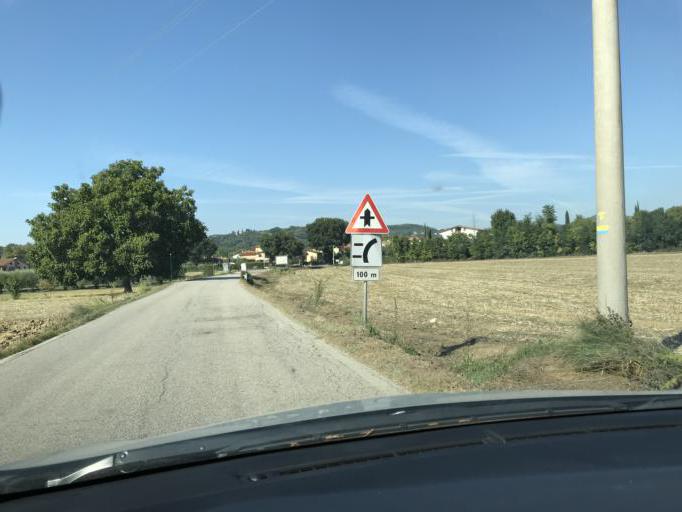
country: IT
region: Umbria
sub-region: Provincia di Perugia
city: Via Lippia
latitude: 43.1070
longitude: 12.4665
